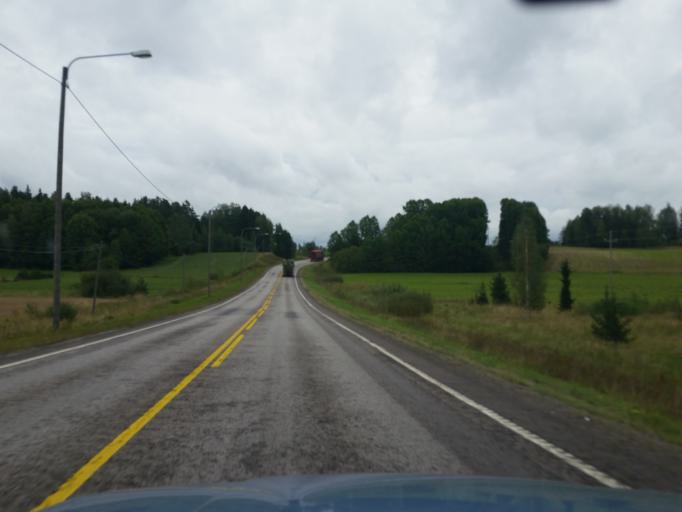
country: FI
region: Uusimaa
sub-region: Helsinki
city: Lohja
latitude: 60.3707
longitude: 24.1395
